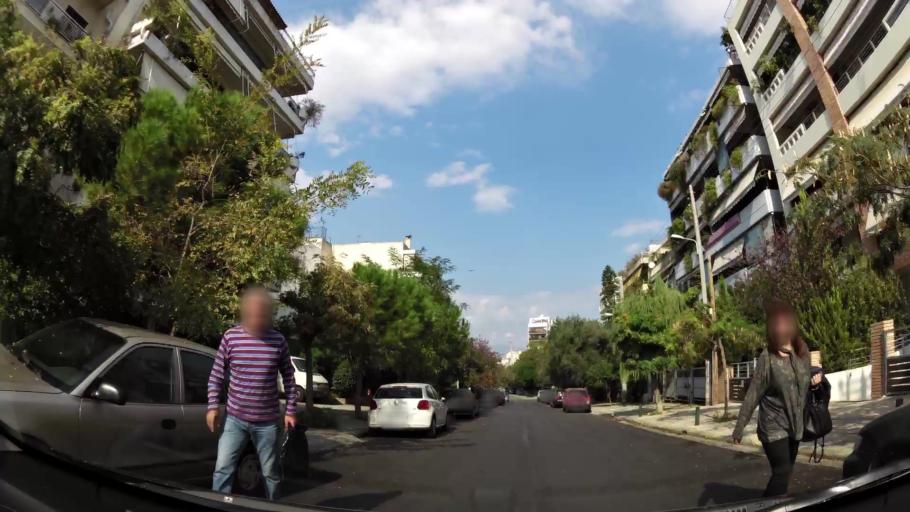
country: GR
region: Attica
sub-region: Nomarchia Athinas
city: Galatsi
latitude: 38.0206
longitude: 23.7416
